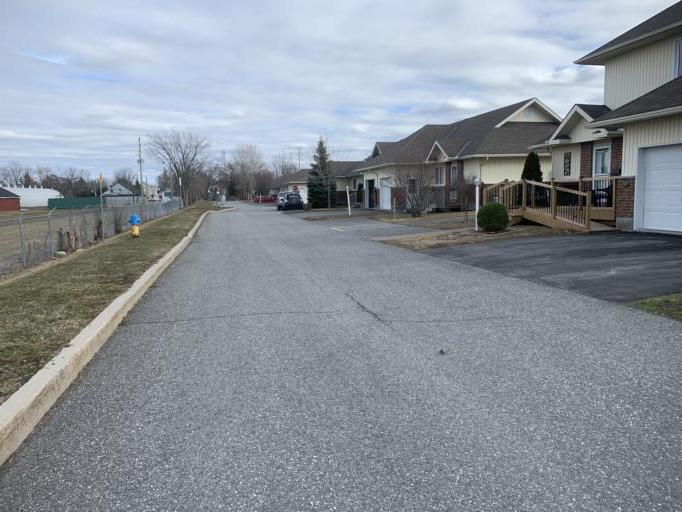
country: CA
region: Ontario
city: Bells Corners
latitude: 45.1959
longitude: -75.8407
